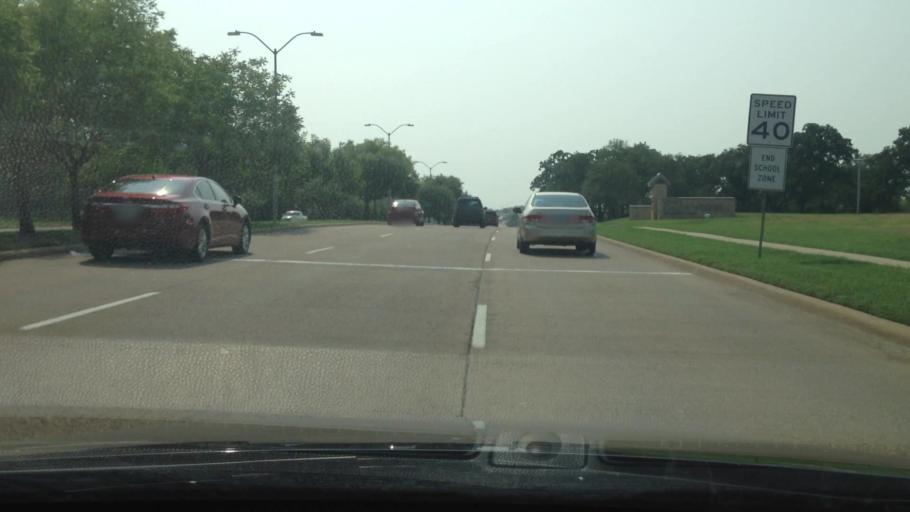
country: US
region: Texas
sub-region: Tarrant County
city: North Richland Hills
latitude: 32.8619
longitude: -97.1955
